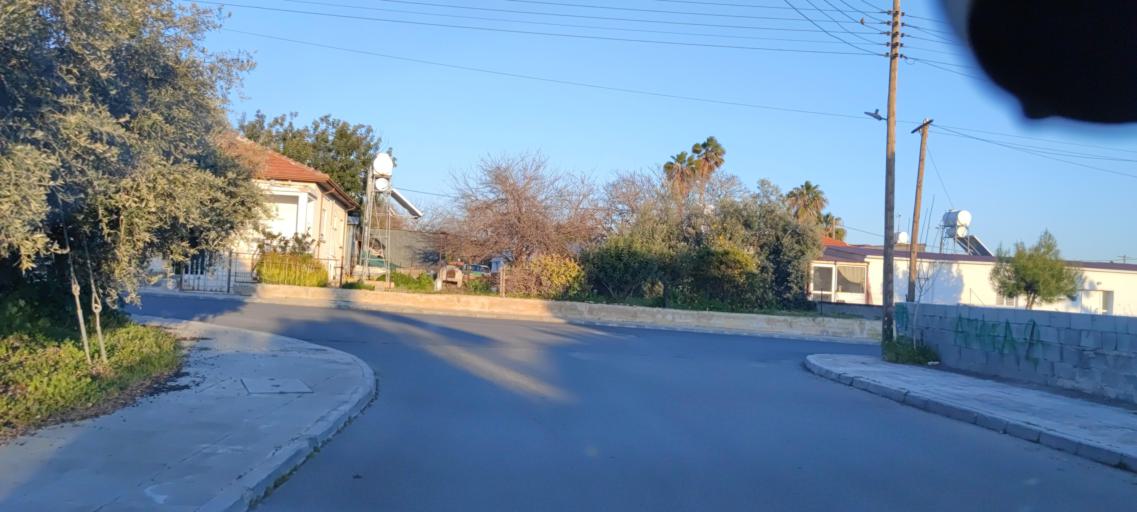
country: CY
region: Pafos
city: Paphos
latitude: 34.7836
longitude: 32.4183
